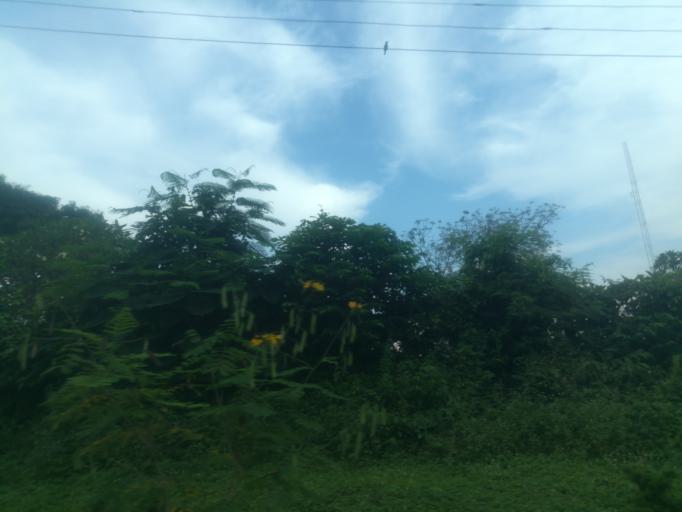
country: NG
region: Oyo
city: Ibadan
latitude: 7.4183
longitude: 3.9054
